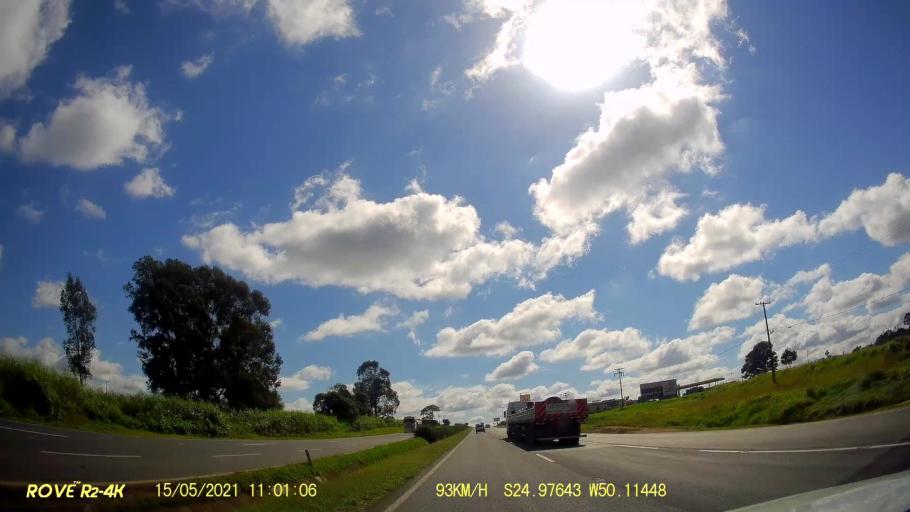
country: BR
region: Parana
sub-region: Carambei
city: Carambei
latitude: -24.9762
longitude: -50.1148
